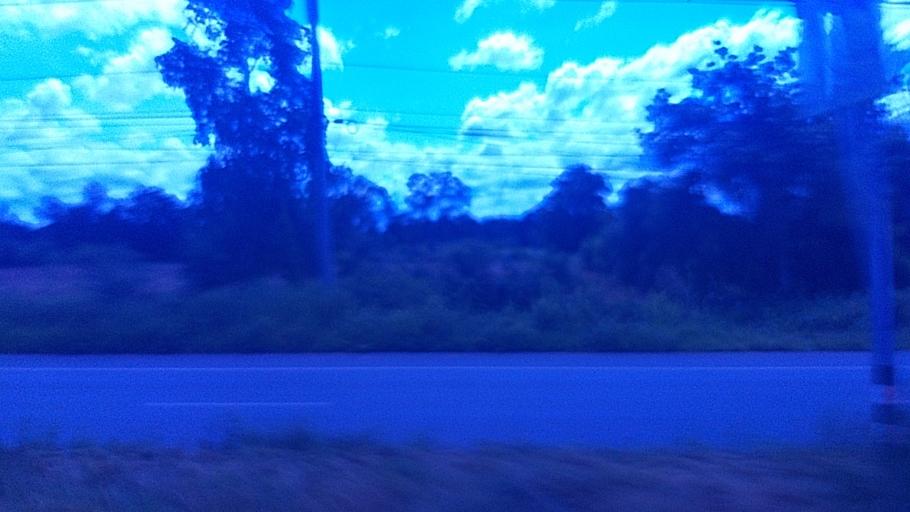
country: TH
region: Nakhon Ratchasima
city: Dan Khun Thot
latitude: 15.1104
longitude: 101.7221
